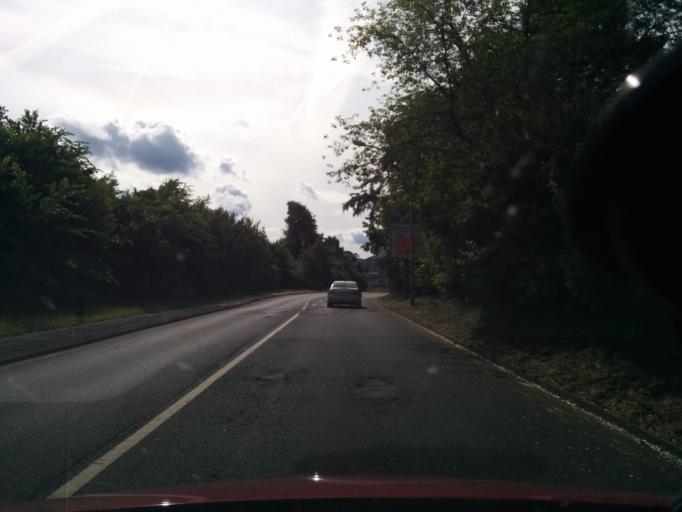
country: DE
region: Lower Saxony
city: Goslar
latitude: 51.9140
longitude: 10.4134
